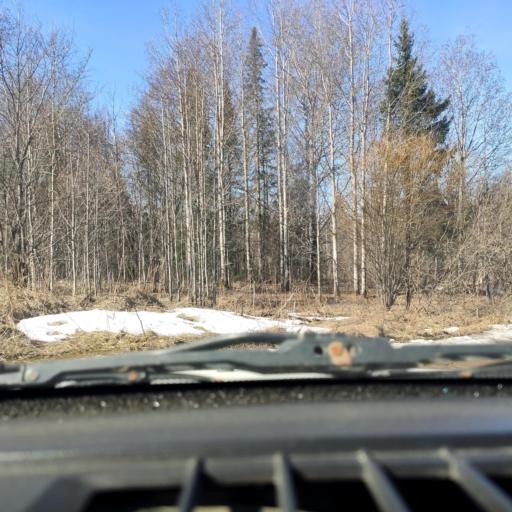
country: RU
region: Perm
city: Kultayevo
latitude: 57.8212
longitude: 55.7996
